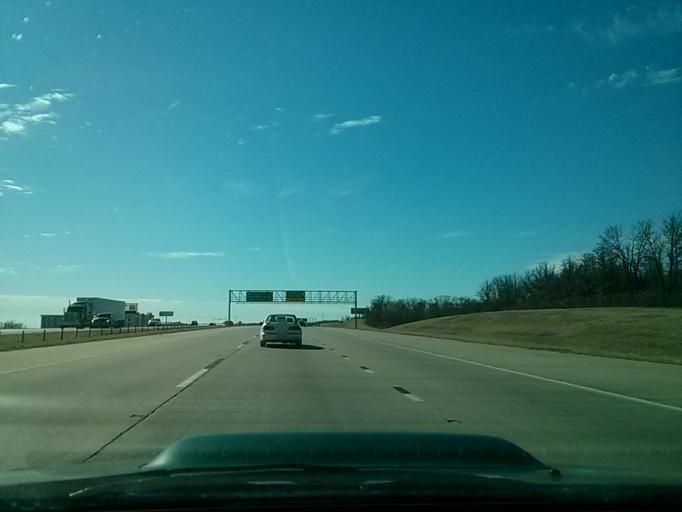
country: US
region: Oklahoma
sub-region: Tulsa County
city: Oakhurst
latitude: 36.0679
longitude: -96.0068
